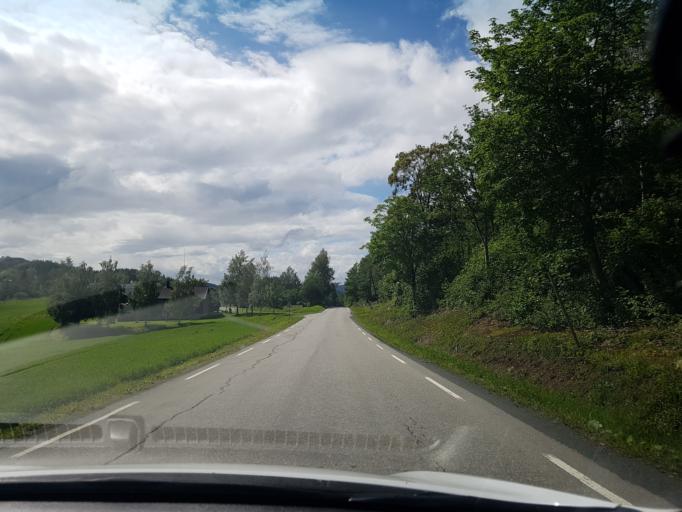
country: NO
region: Nord-Trondelag
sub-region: Stjordal
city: Stjordalshalsen
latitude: 63.5905
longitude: 11.0054
